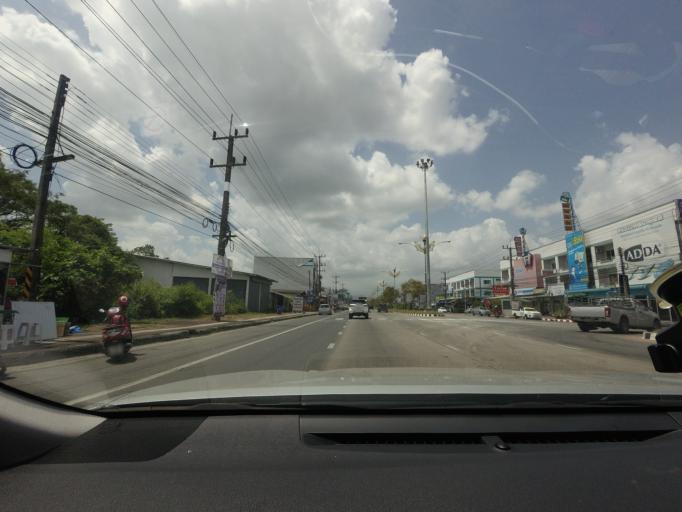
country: TH
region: Nakhon Si Thammarat
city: Nakhon Si Thammarat
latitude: 8.4340
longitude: 99.9266
